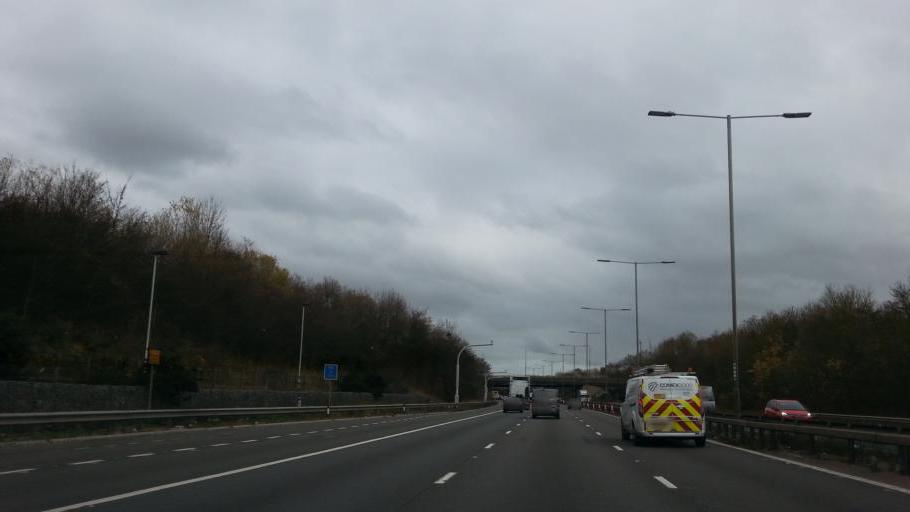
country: GB
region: England
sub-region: Warwickshire
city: Water Orton
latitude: 52.5050
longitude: -1.7419
